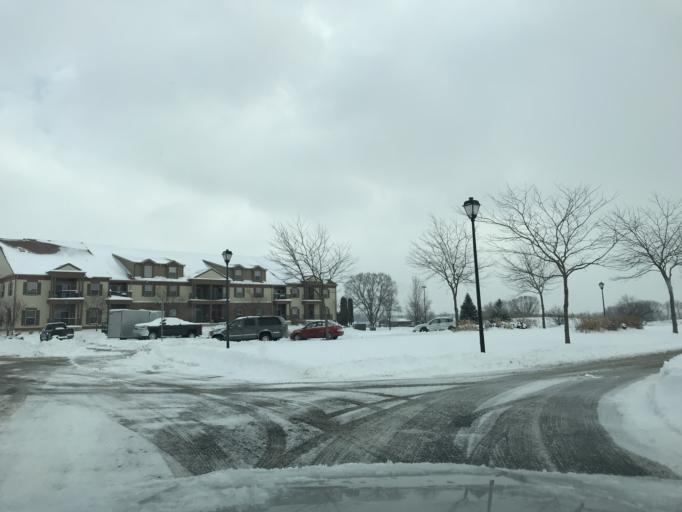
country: US
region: Wisconsin
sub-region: Dane County
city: Sun Prairie
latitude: 43.1659
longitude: -89.2774
